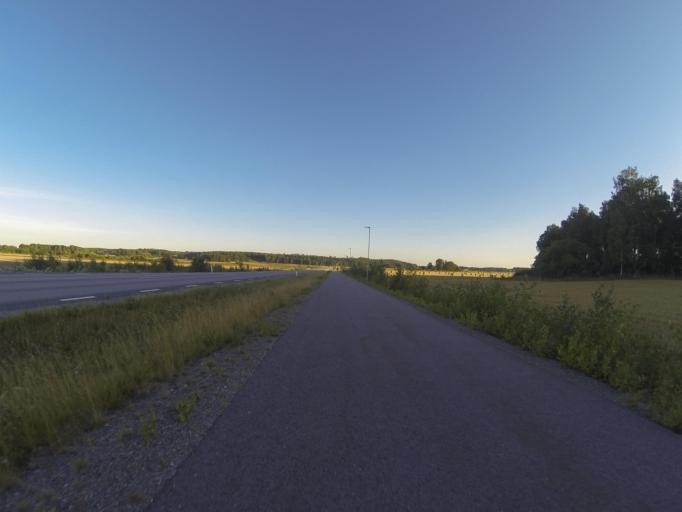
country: SE
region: Vaestmanland
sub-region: Vasteras
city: Tillberga
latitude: 59.5899
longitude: 16.6663
